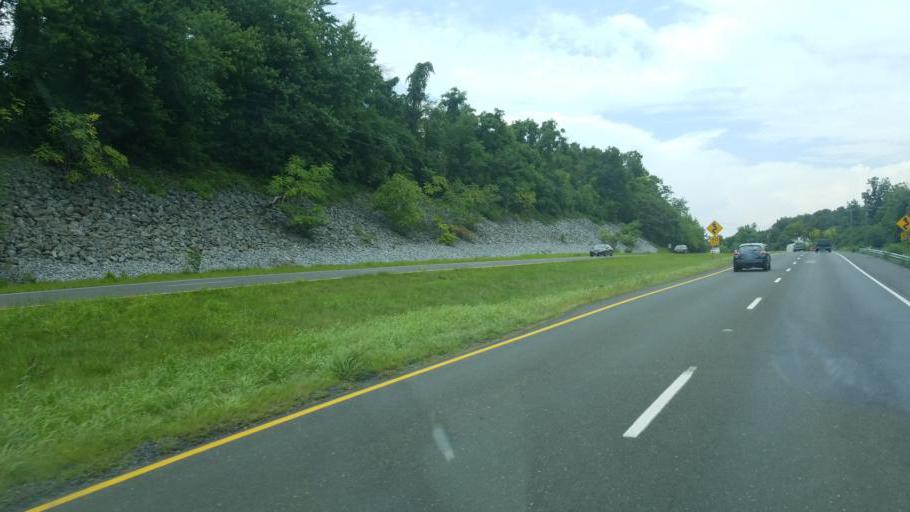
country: US
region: Virginia
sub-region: City of Winchester
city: Winchester
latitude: 39.2360
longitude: -78.1998
